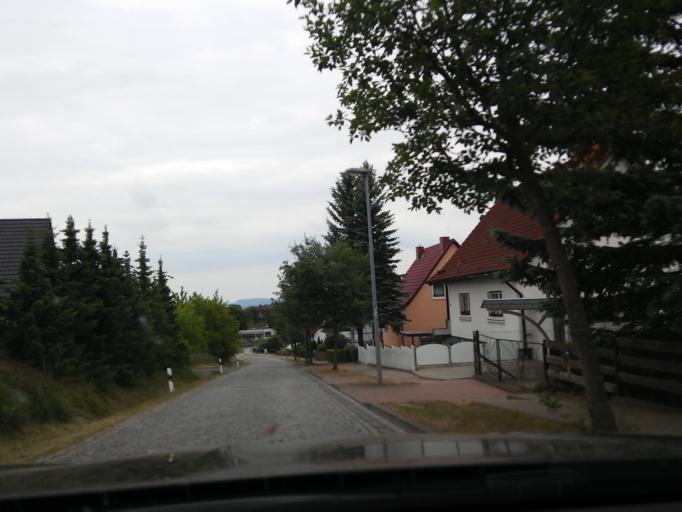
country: DE
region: Thuringia
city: Sondershausen
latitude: 51.3724
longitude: 10.8442
